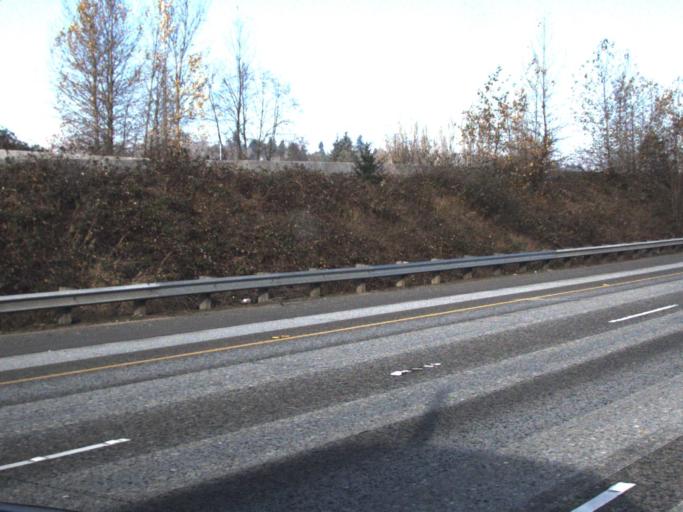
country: US
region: Washington
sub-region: King County
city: Tukwila
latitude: 47.4601
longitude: -122.2633
